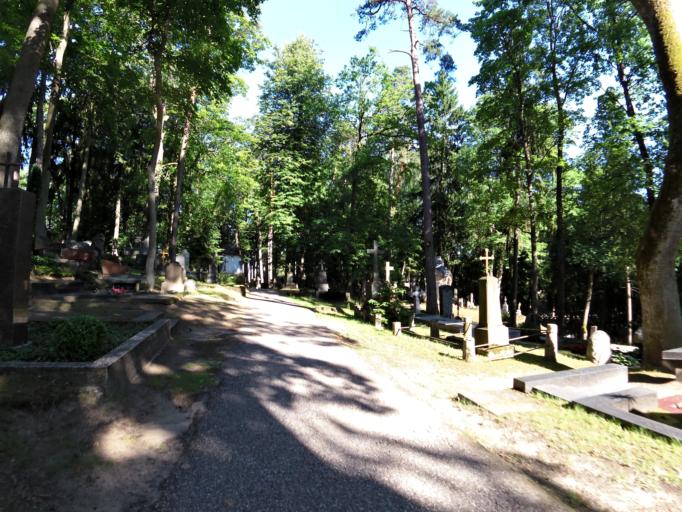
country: LT
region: Vilnius County
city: Rasos
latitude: 54.6984
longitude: 25.3202
